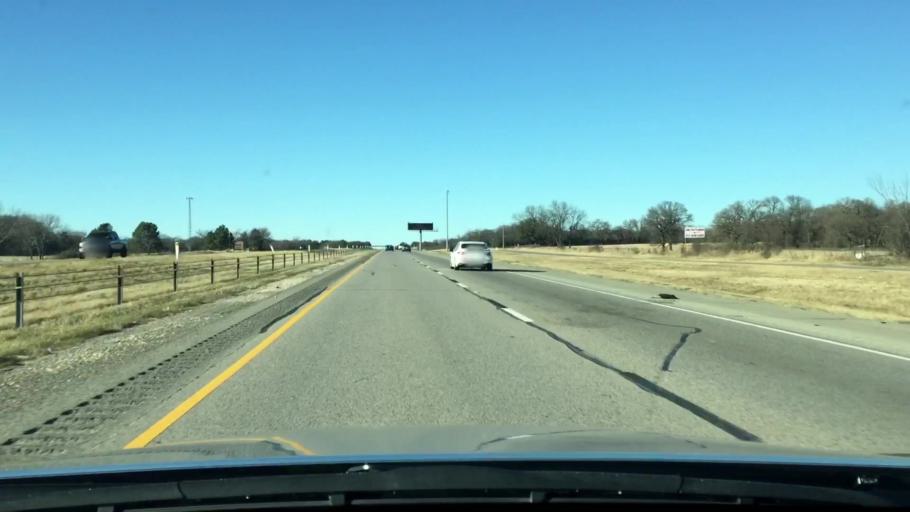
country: US
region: Texas
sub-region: Johnson County
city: Alvarado
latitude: 32.3654
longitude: -97.2005
